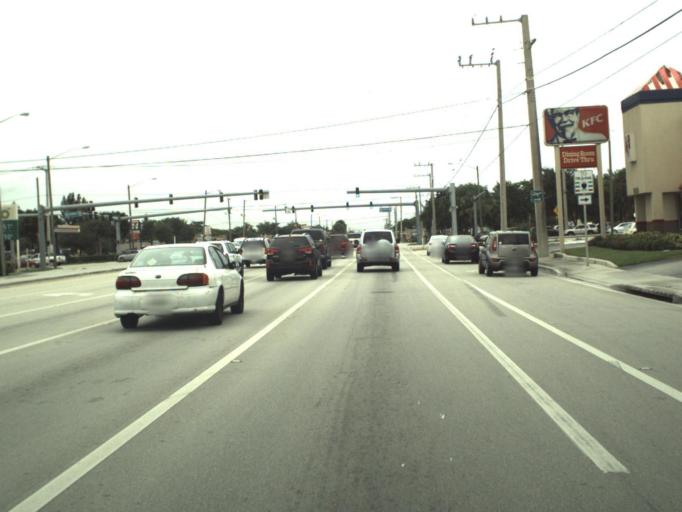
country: US
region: Florida
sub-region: Palm Beach County
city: Haverhill
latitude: 26.6909
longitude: -80.1115
